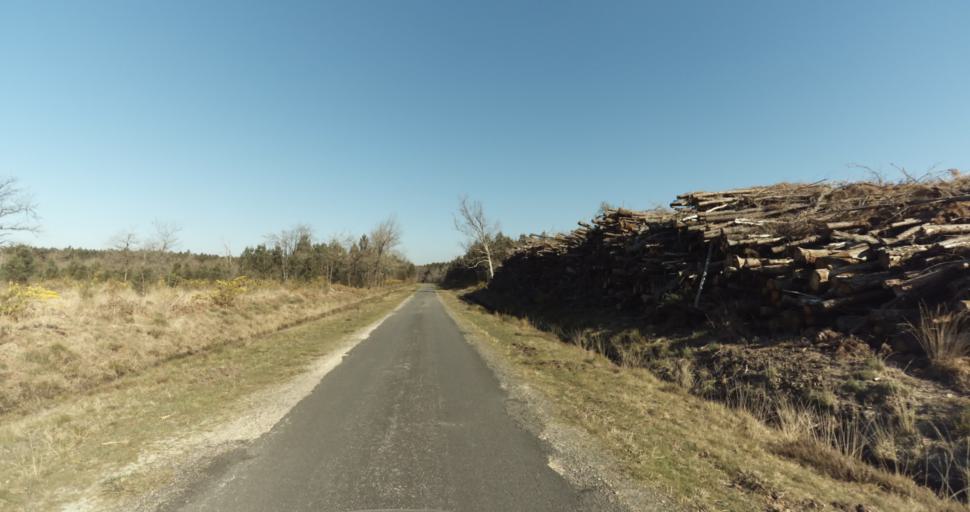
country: FR
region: Aquitaine
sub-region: Departement de la Gironde
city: Martignas-sur-Jalle
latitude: 44.8104
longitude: -0.8521
